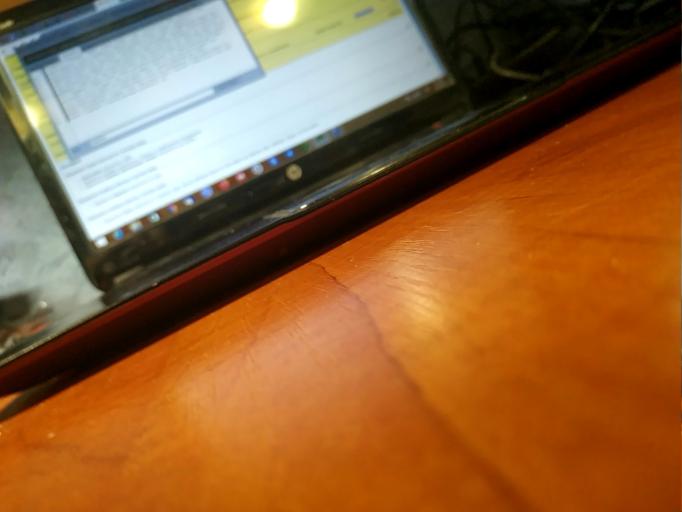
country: RU
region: Vologda
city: Ustyuzhna
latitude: 58.6623
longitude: 36.4250
